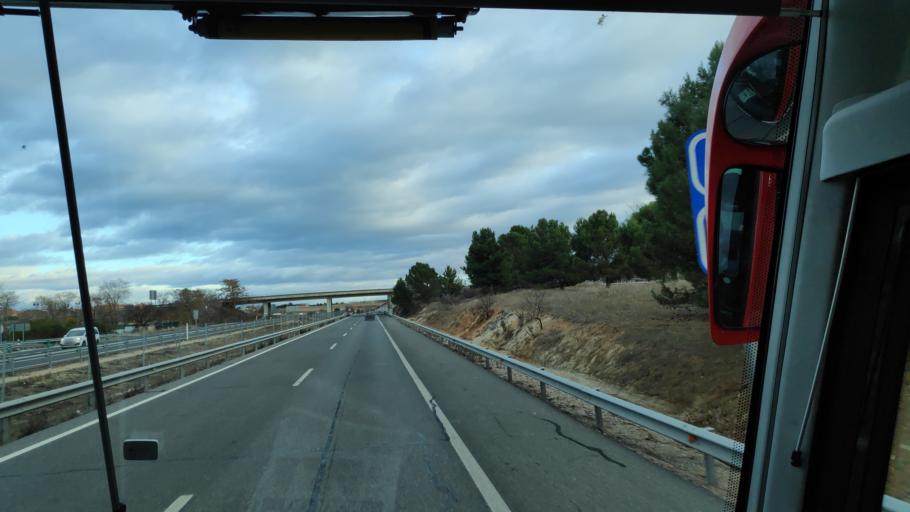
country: ES
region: Madrid
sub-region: Provincia de Madrid
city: Villarejo de Salvanes
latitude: 40.1668
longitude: -3.2846
